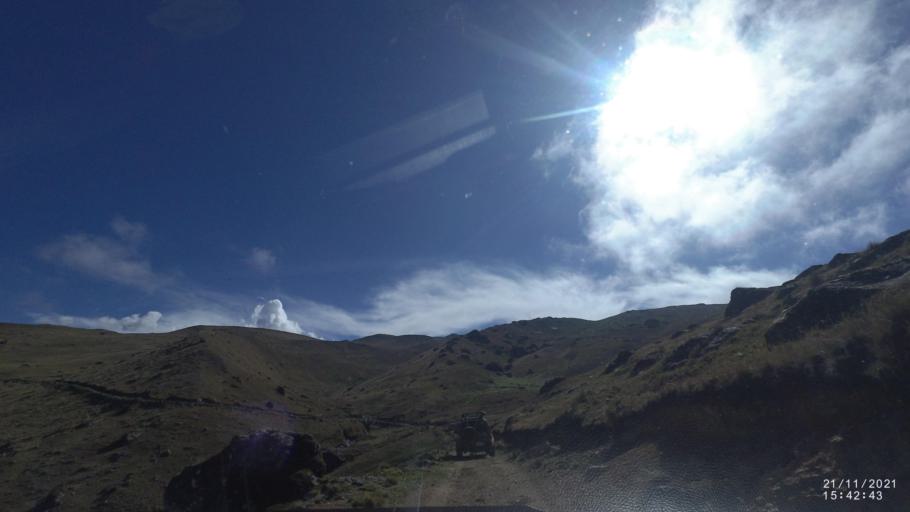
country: BO
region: Cochabamba
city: Cochabamba
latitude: -16.9652
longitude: -66.2695
